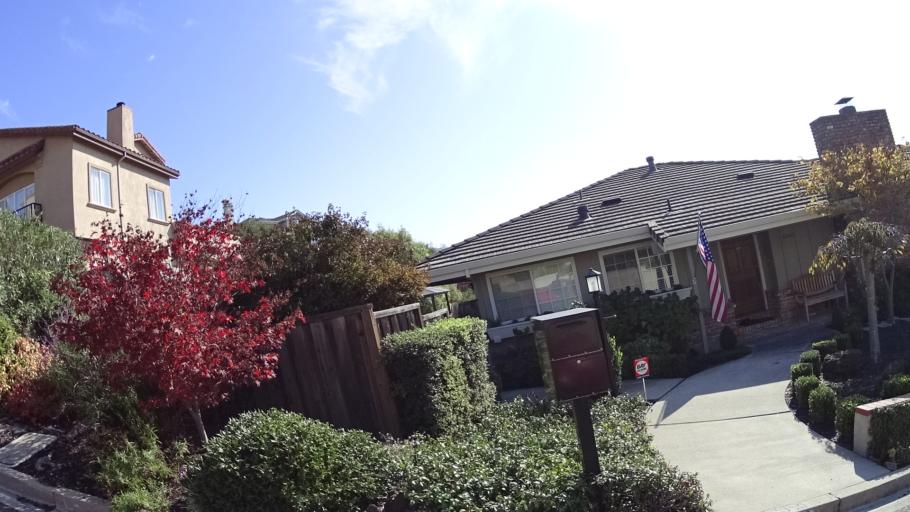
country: US
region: California
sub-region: Alameda County
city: Piedmont
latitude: 37.8449
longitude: -122.2244
